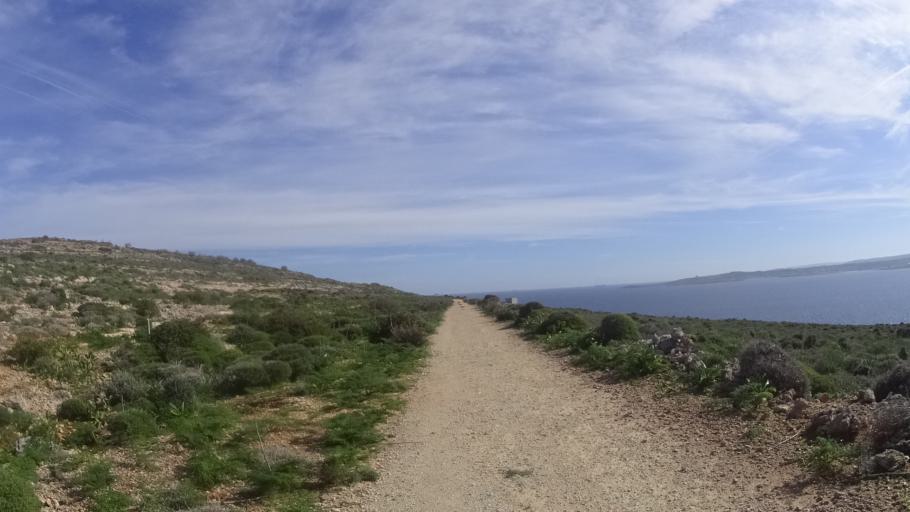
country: MT
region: Il-Qala
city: Qala
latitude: 36.0063
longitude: 14.3379
